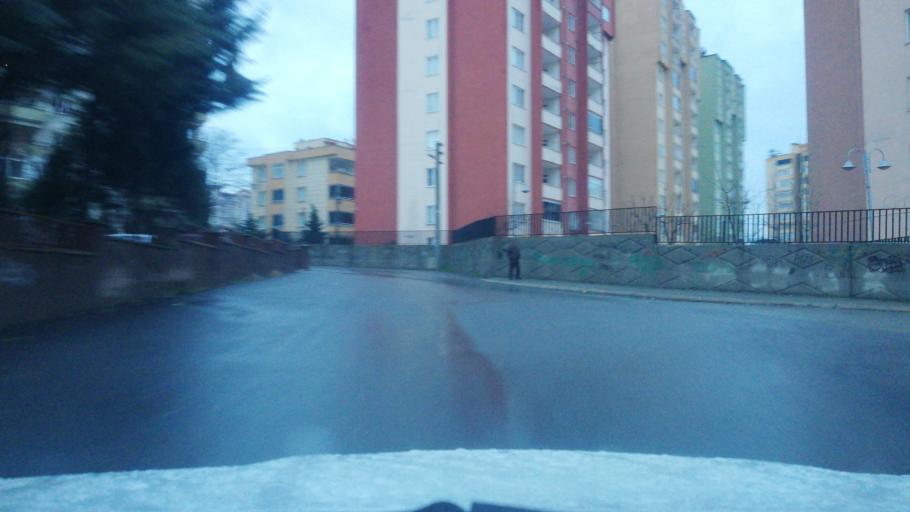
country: TR
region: Kahramanmaras
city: Kahramanmaras
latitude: 37.5953
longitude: 36.8999
